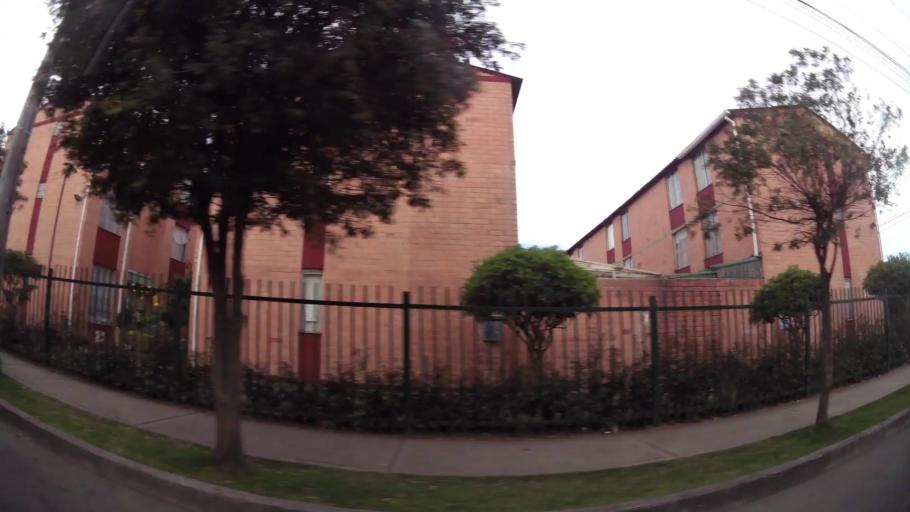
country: CO
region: Cundinamarca
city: Mosquera
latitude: 4.7088
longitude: -74.2240
